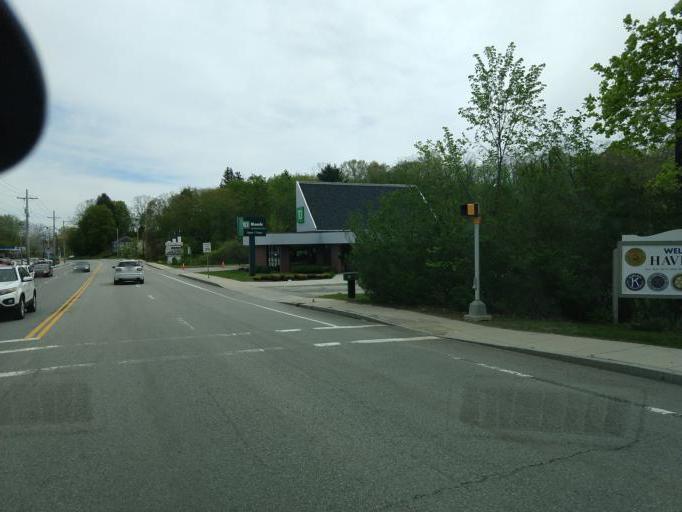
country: US
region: Massachusetts
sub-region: Essex County
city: Haverhill
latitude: 42.7554
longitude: -71.1036
